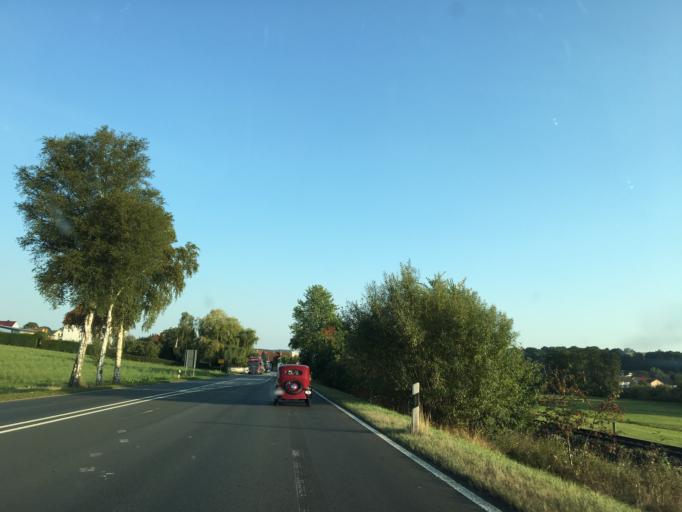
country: DE
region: Hesse
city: Wetter
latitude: 50.8947
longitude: 8.7425
